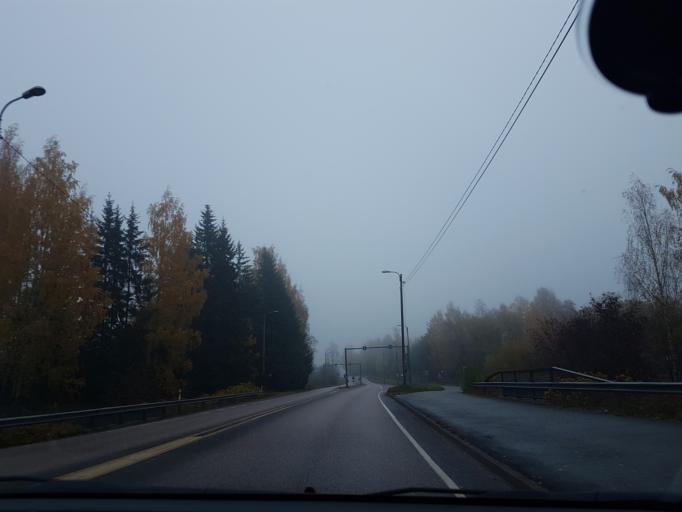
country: FI
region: Uusimaa
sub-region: Helsinki
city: Tuusula
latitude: 60.4107
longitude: 25.0430
